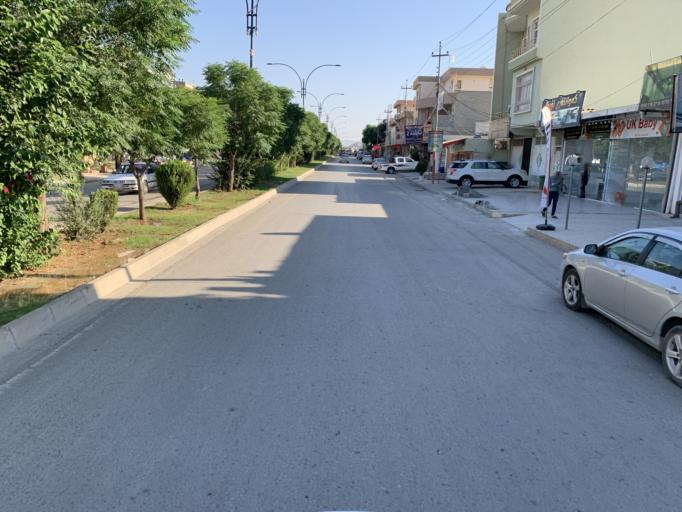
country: IQ
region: As Sulaymaniyah
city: Raniye
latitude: 36.2509
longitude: 44.8767
